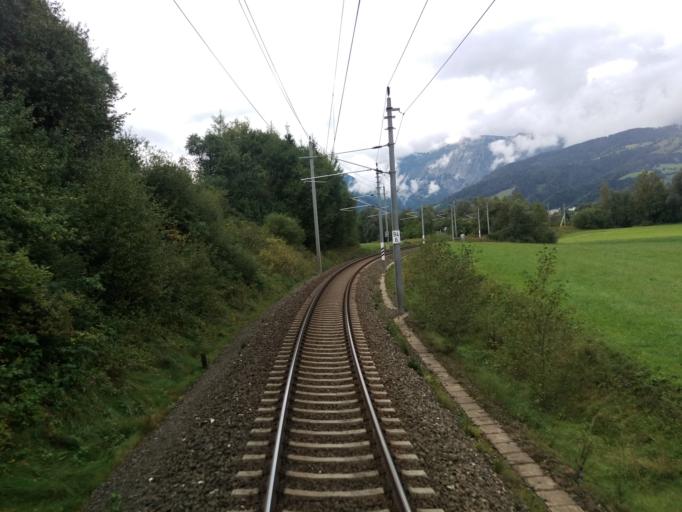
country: AT
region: Styria
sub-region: Politischer Bezirk Liezen
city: Liezen
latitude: 47.5509
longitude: 14.2599
